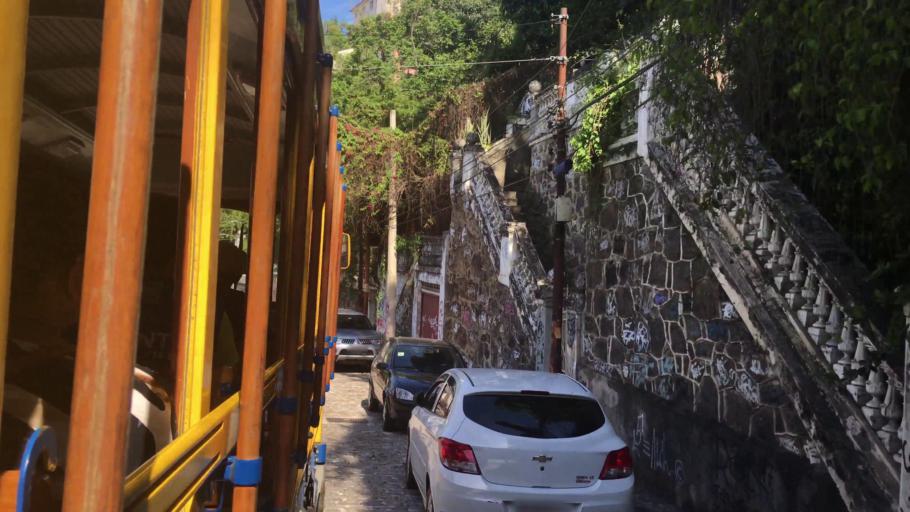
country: BR
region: Rio de Janeiro
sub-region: Rio De Janeiro
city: Rio de Janeiro
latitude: -22.9168
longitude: -43.1823
